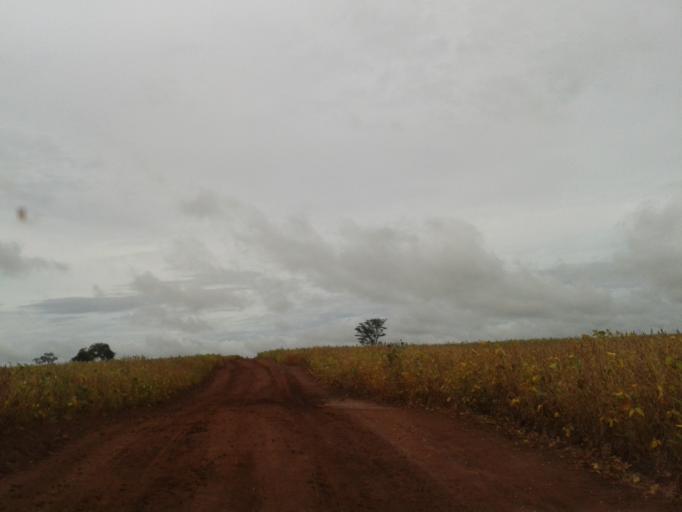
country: BR
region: Minas Gerais
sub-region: Capinopolis
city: Capinopolis
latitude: -18.7433
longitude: -49.7761
